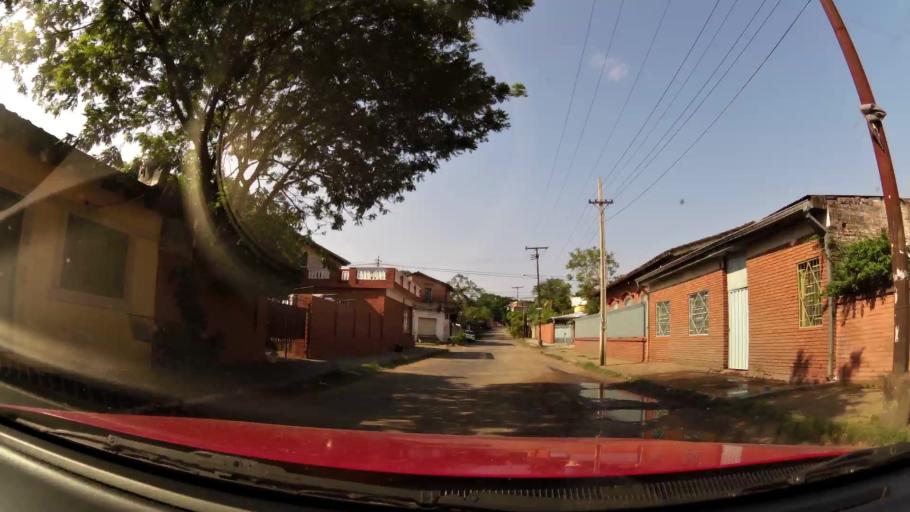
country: PY
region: Asuncion
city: Asuncion
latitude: -25.3135
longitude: -57.6369
